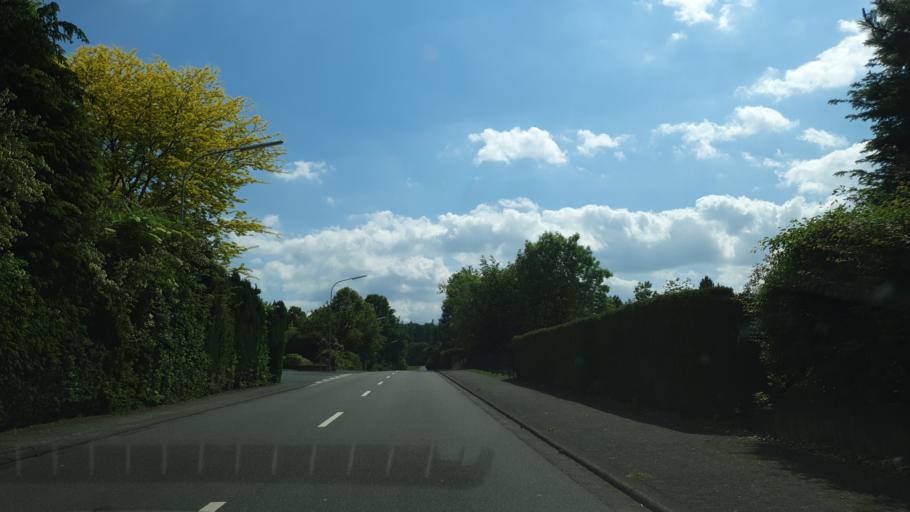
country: DE
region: Rheinland-Pfalz
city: Helferskirchen
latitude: 50.5095
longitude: 7.8117
